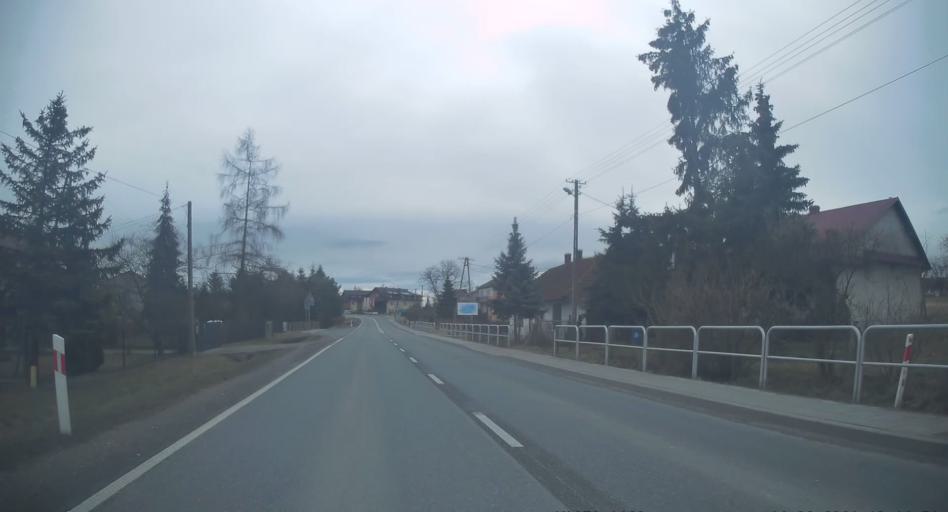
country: PL
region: Lesser Poland Voivodeship
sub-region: Powiat wielicki
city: Szarow
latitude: 50.0024
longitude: 20.2685
